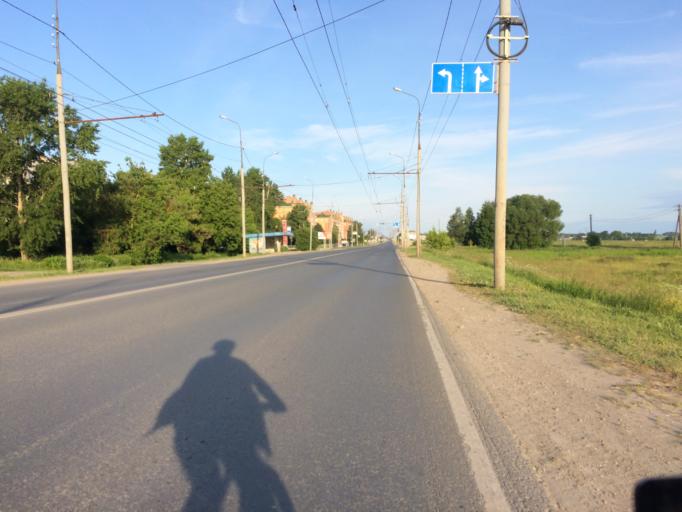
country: RU
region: Mariy-El
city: Medvedevo
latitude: 56.6392
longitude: 47.8055
